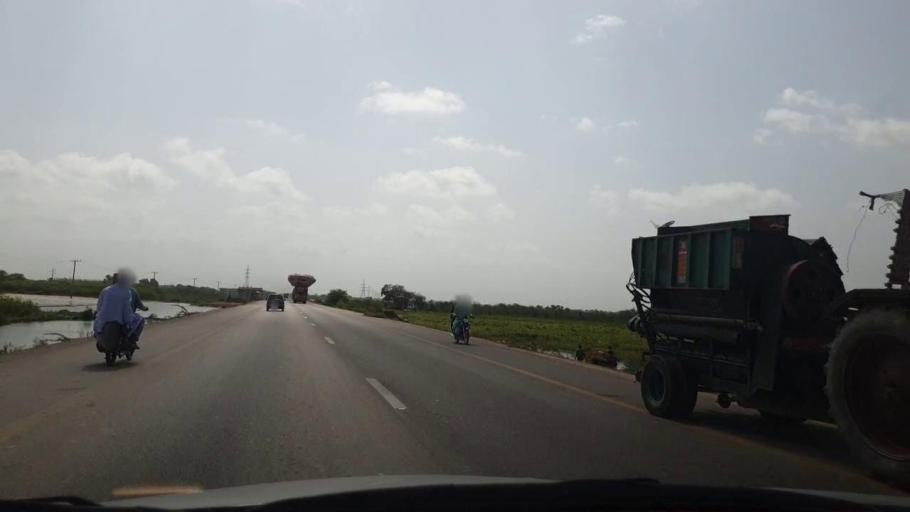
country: PK
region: Sindh
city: Talhar
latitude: 24.9292
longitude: 68.7148
